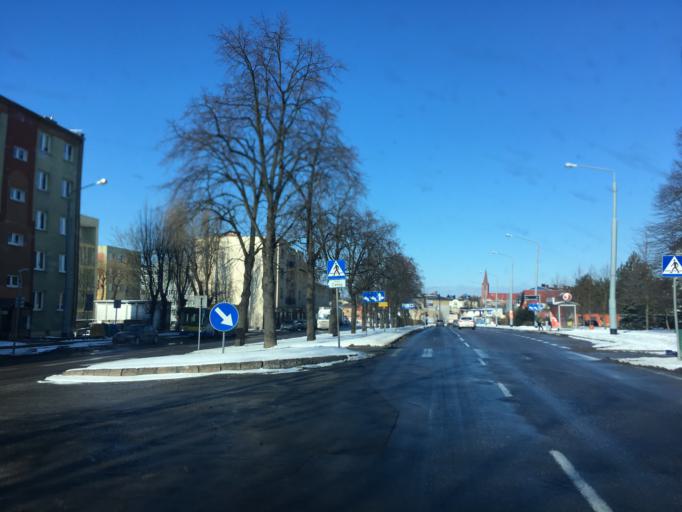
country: PL
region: Pomeranian Voivodeship
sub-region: Slupsk
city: Slupsk
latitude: 54.4635
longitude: 17.0420
